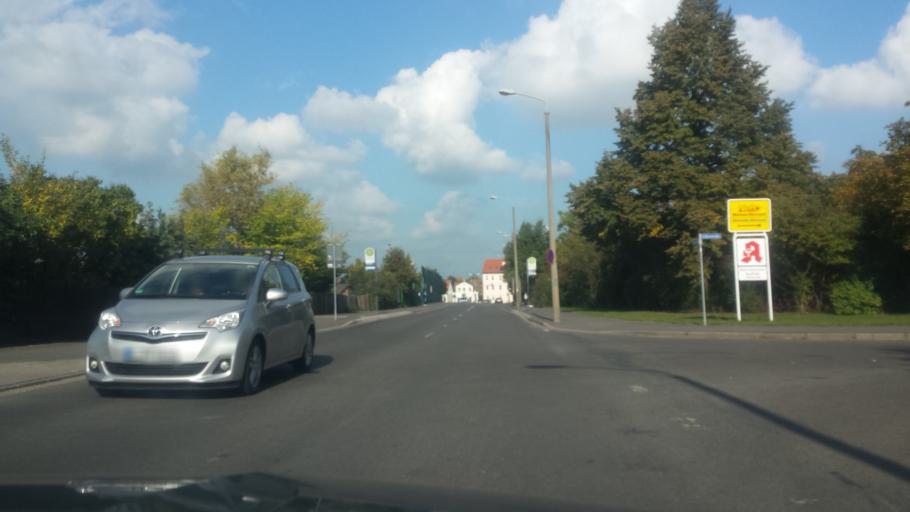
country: DE
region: Saxony
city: Taucha
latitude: 51.3773
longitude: 12.4302
